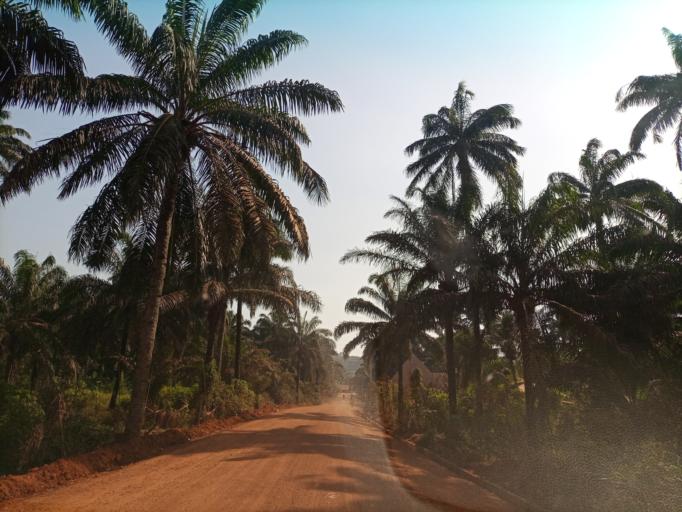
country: NG
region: Enugu
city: Aku
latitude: 6.7043
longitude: 7.3212
